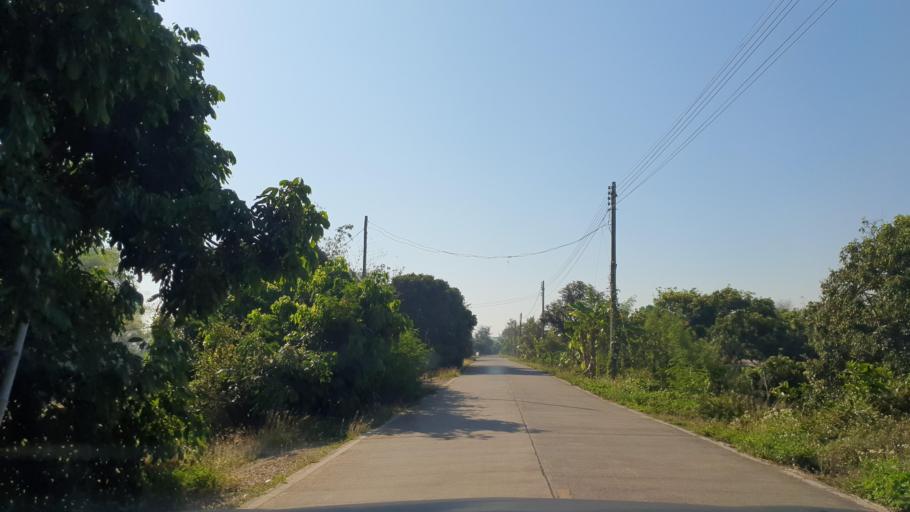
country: TH
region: Chiang Mai
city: Saraphi
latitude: 18.6917
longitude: 99.0787
